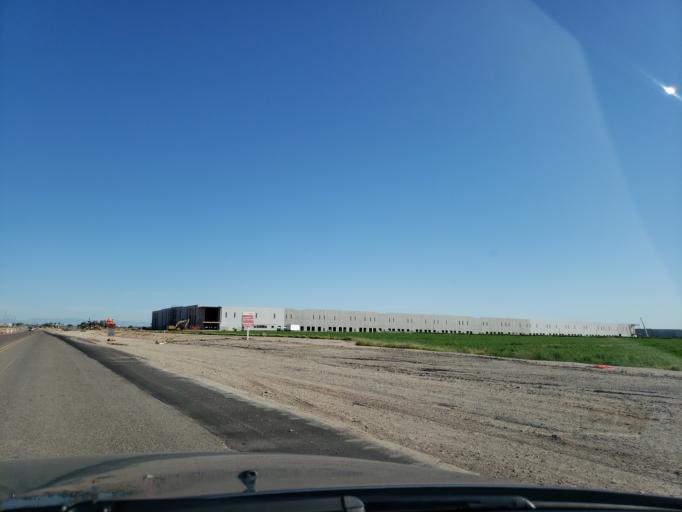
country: US
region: Arizona
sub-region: Maricopa County
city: Goodyear
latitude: 33.4402
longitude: -112.3755
